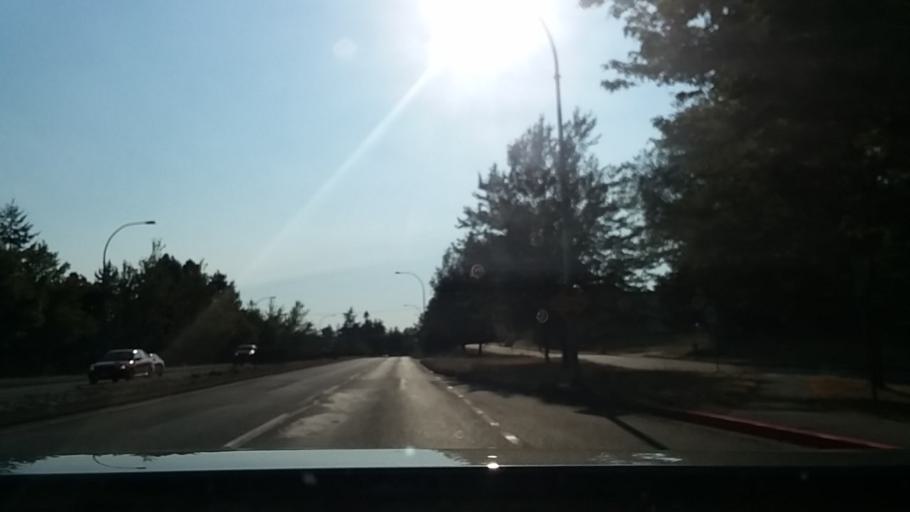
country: CA
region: British Columbia
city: Victoria
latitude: 48.4668
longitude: -123.3891
